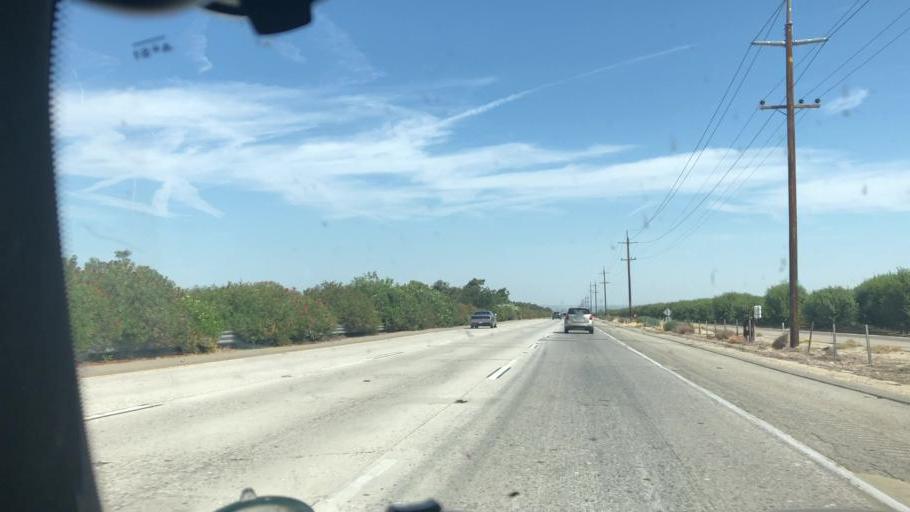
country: US
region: California
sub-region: Kern County
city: Weedpatch
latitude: 35.0353
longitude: -118.9606
